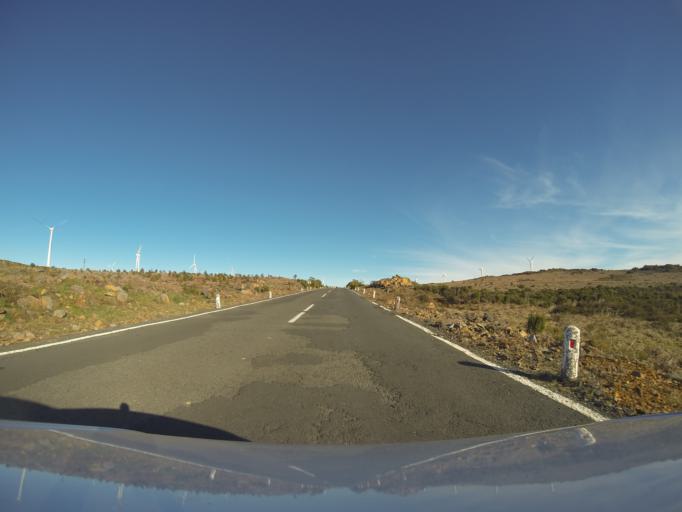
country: PT
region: Madeira
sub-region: Sao Vicente
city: Sao Vicente
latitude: 32.7636
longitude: -17.0710
